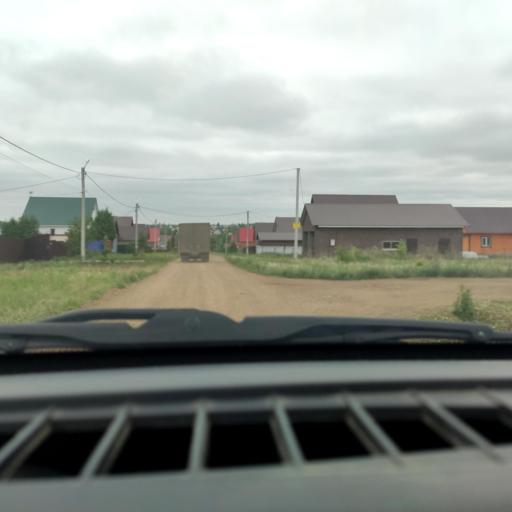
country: RU
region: Bashkortostan
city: Iglino
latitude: 54.8334
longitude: 56.4493
